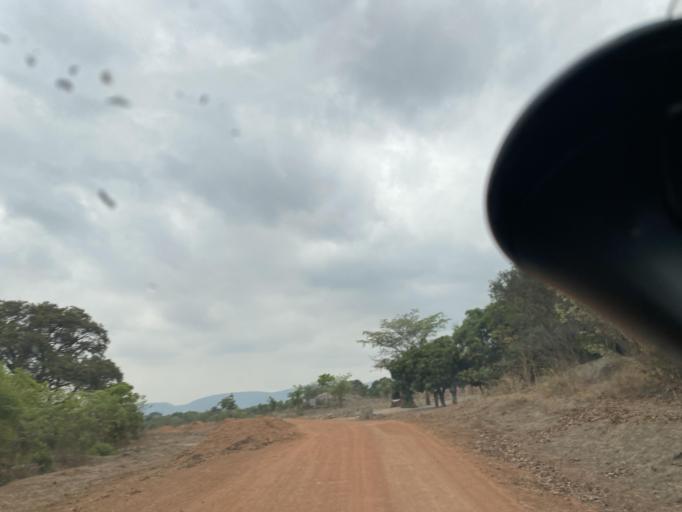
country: ZM
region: Lusaka
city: Chongwe
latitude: -15.2382
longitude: 28.7192
